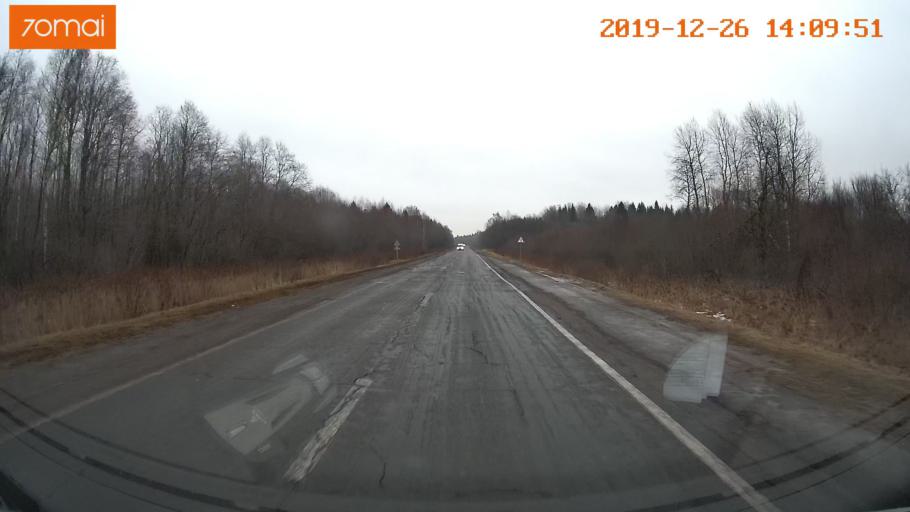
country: RU
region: Jaroslavl
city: Poshekhon'ye
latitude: 58.5085
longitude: 38.9416
